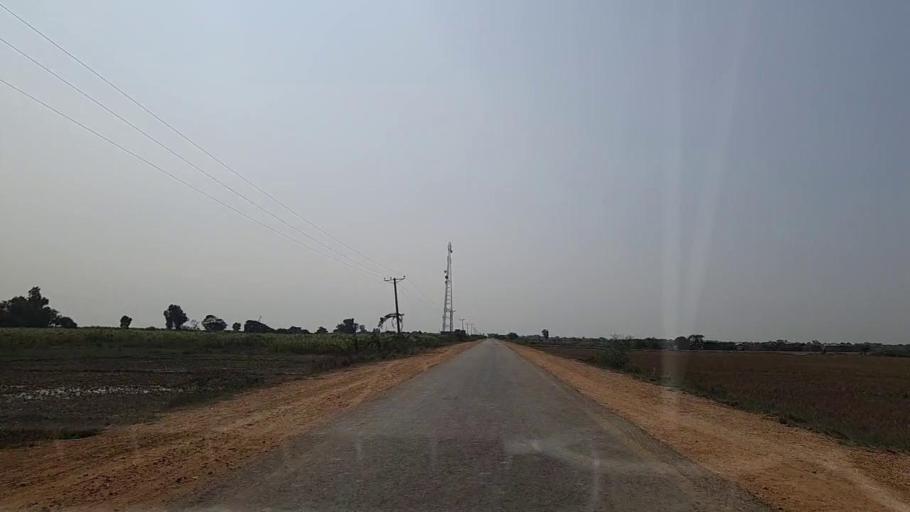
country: PK
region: Sindh
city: Chuhar Jamali
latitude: 24.2867
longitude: 67.9236
